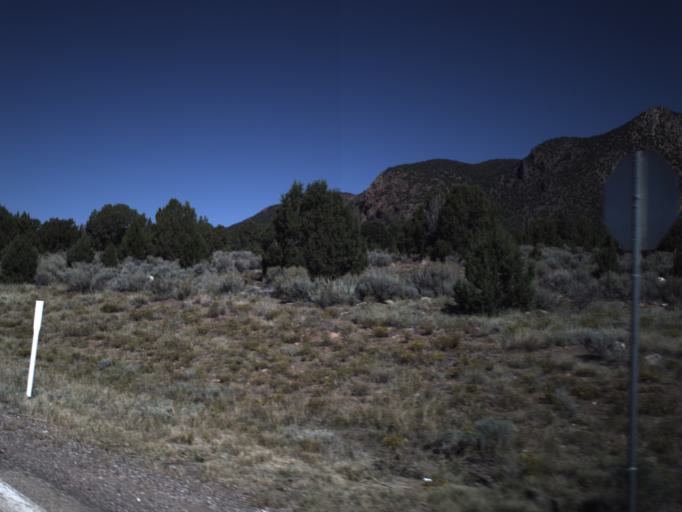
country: US
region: Utah
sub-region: Washington County
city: Enterprise
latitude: 37.6610
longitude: -113.4617
